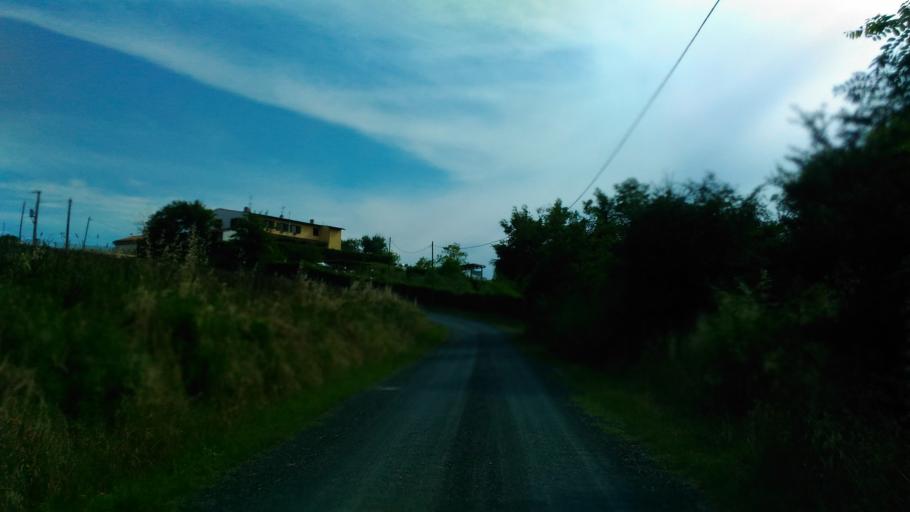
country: IT
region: Tuscany
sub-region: Province of Pisa
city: Orciano Pisano
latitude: 43.4492
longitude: 10.5216
